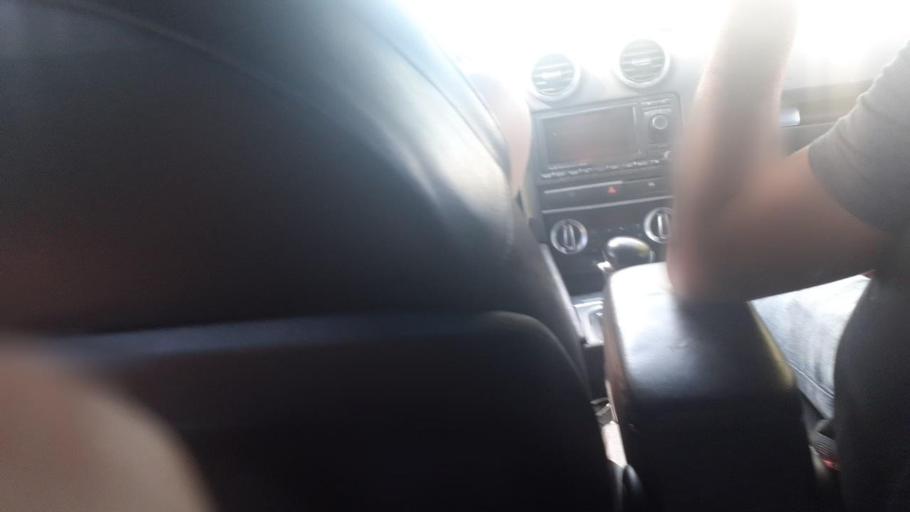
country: FR
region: Haute-Normandie
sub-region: Departement de la Seine-Maritime
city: Grand-Couronne
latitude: 49.3644
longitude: 1.0162
